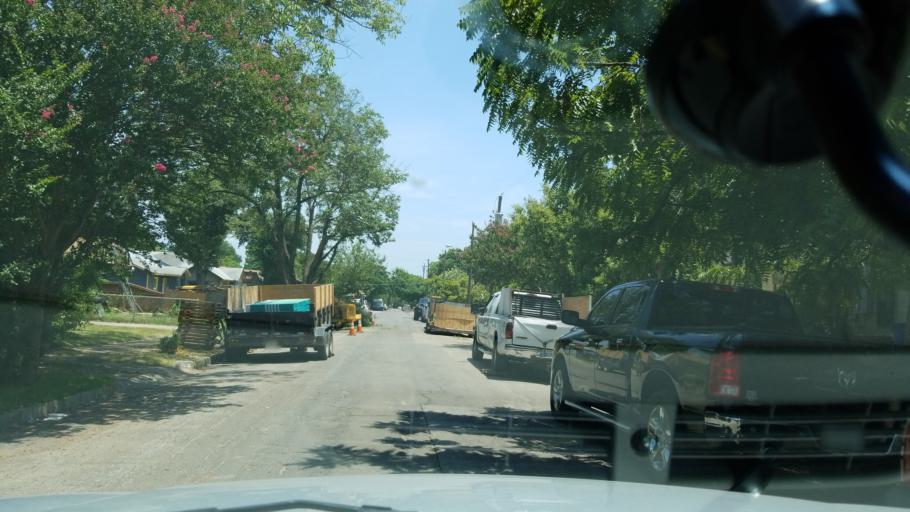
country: US
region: Texas
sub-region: Dallas County
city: Cockrell Hill
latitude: 32.7281
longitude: -96.8675
